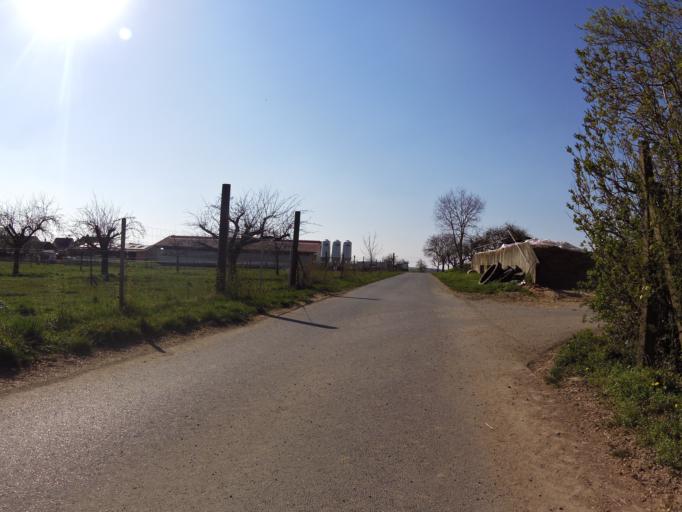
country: DE
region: Bavaria
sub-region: Regierungsbezirk Unterfranken
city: Prosselsheim
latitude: 49.8250
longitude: 10.1048
